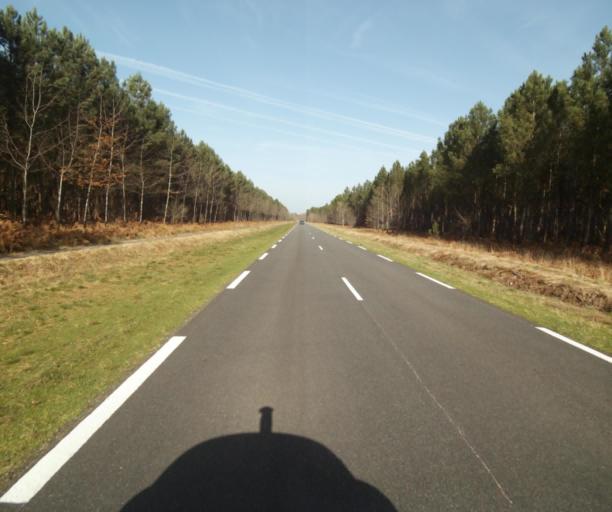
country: FR
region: Aquitaine
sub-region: Departement de la Gironde
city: Grignols
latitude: 44.1893
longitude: -0.1130
